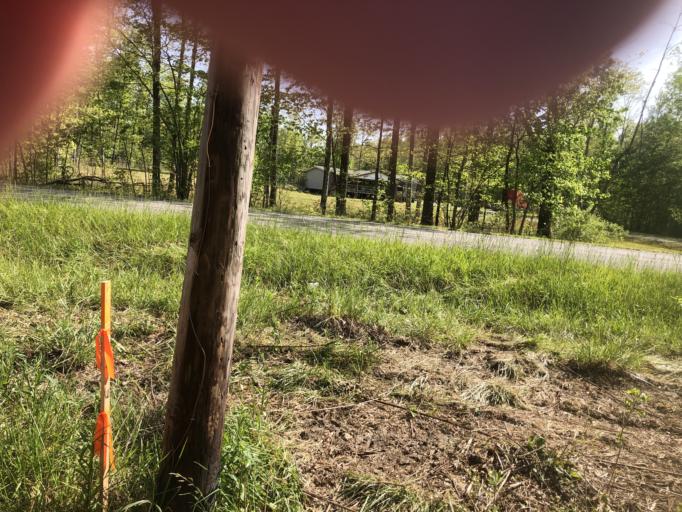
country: US
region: Tennessee
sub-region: Fentress County
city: Grimsley
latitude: 36.3127
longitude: -84.8538
